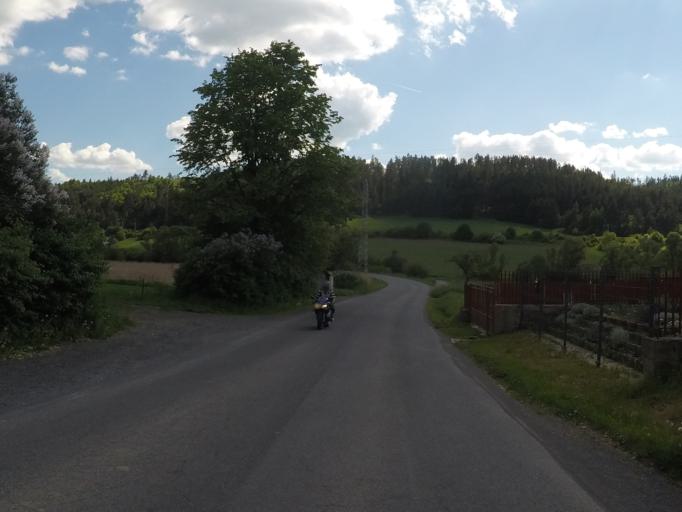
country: SK
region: Presovsky
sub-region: Okres Poprad
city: Poprad
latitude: 49.0126
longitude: 20.3763
